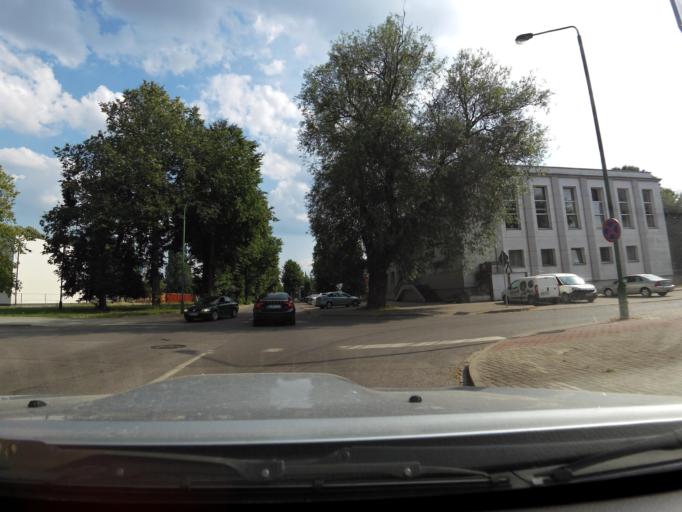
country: LT
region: Klaipedos apskritis
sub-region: Klaipeda
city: Klaipeda
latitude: 55.7003
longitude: 21.1409
